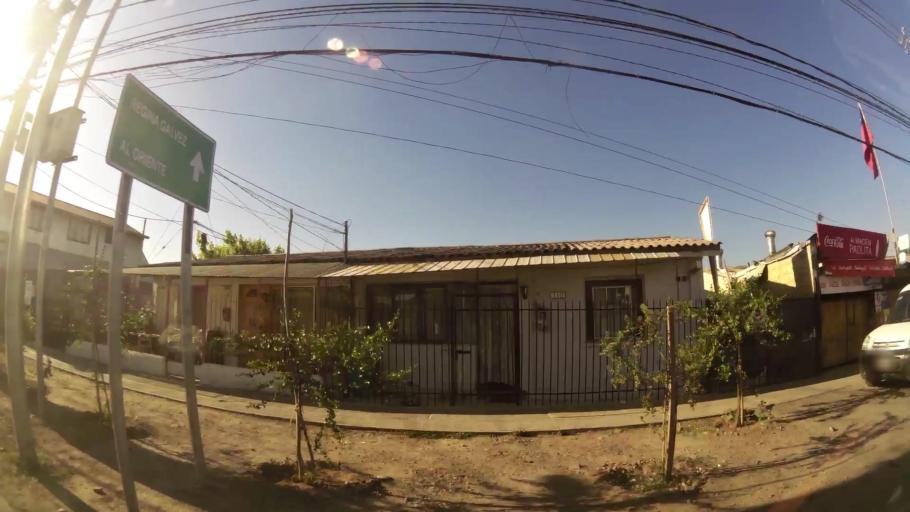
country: CL
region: Santiago Metropolitan
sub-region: Provincia de Maipo
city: San Bernardo
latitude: -33.6377
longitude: -70.7094
